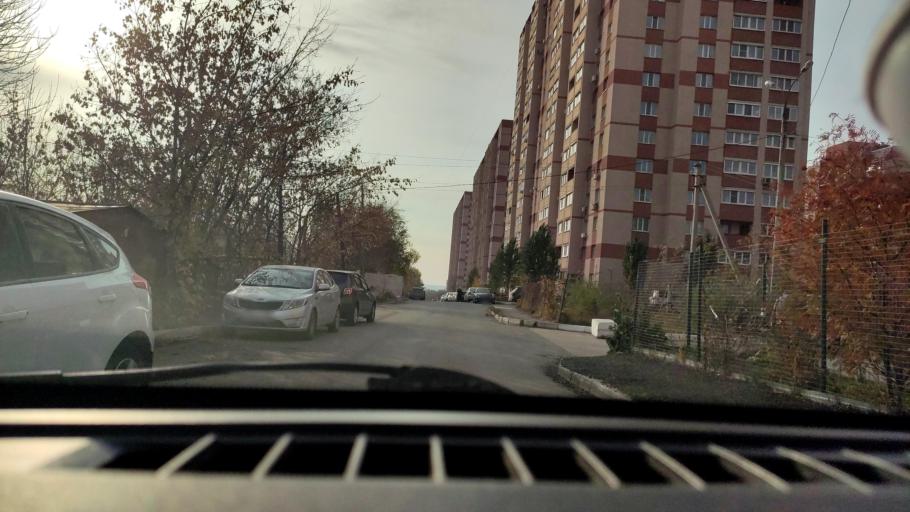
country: RU
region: Samara
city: Samara
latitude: 53.2103
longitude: 50.2082
